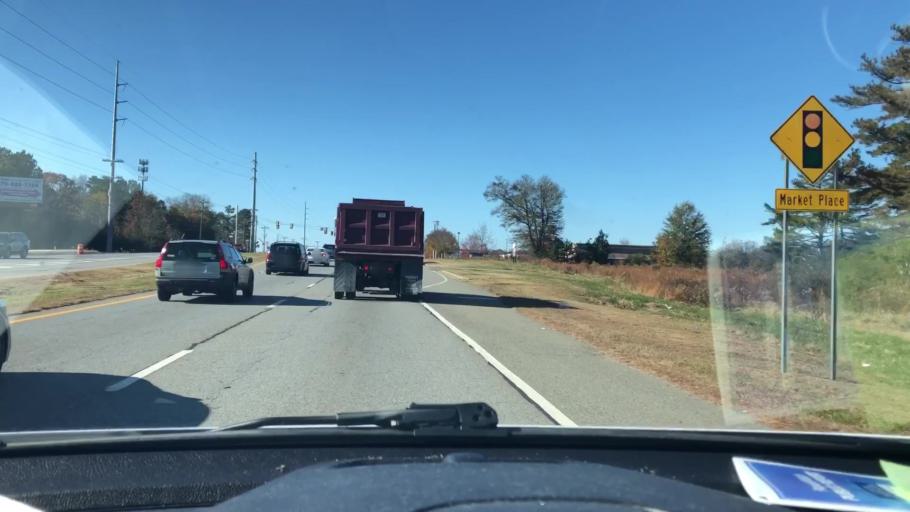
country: US
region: Georgia
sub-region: Fulton County
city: Johns Creek
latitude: 34.0928
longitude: -84.1715
